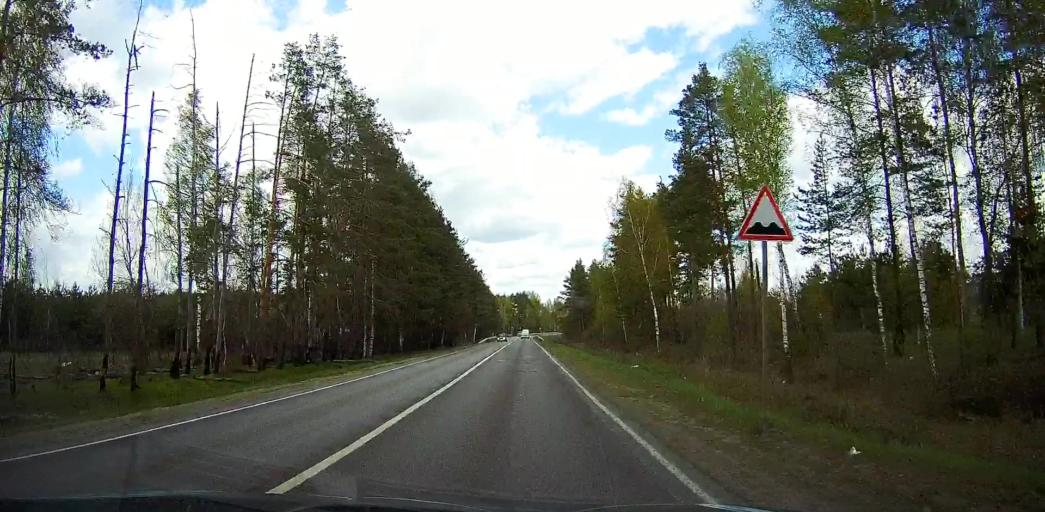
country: RU
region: Moskovskaya
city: Davydovo
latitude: 55.6277
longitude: 38.8618
